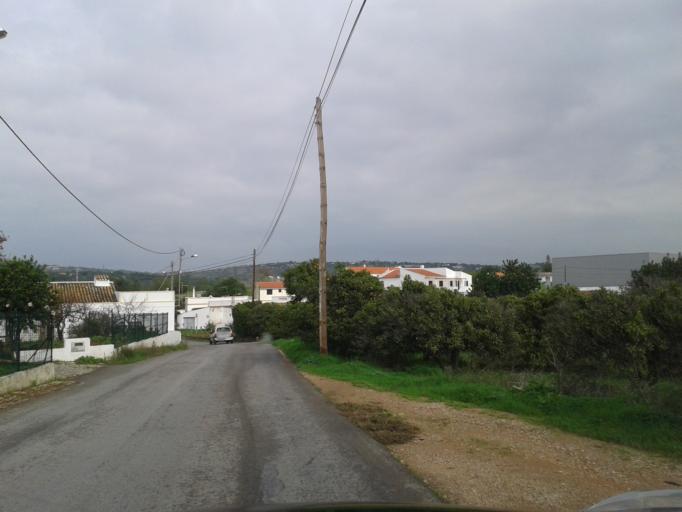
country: PT
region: Faro
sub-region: Loule
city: Boliqueime
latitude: 37.1209
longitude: -8.1883
